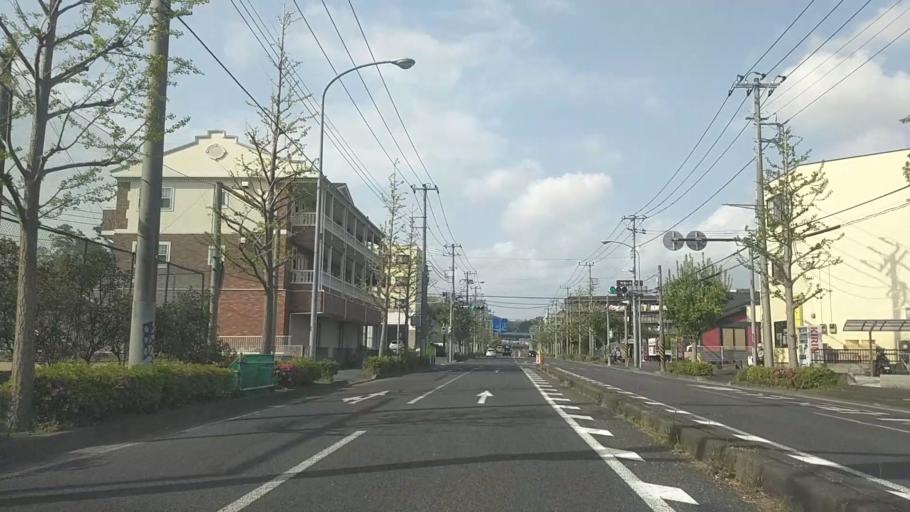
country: JP
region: Kanagawa
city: Kamakura
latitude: 35.3743
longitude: 139.5514
